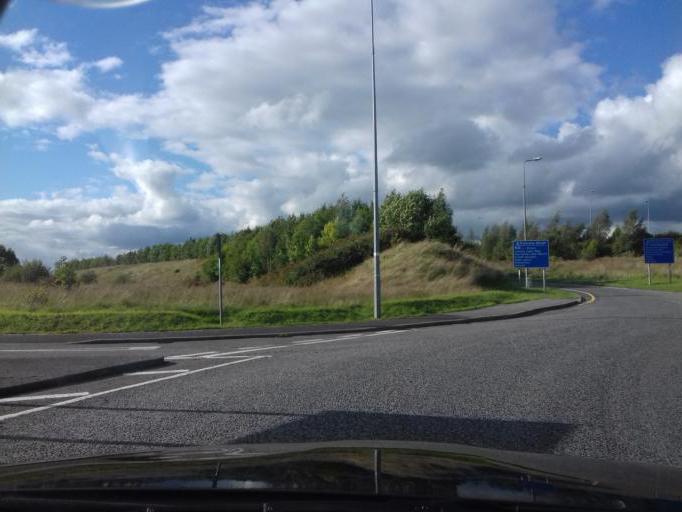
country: IE
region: Leinster
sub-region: An Iarmhi
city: Kilbeggan
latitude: 53.3573
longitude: -7.4956
